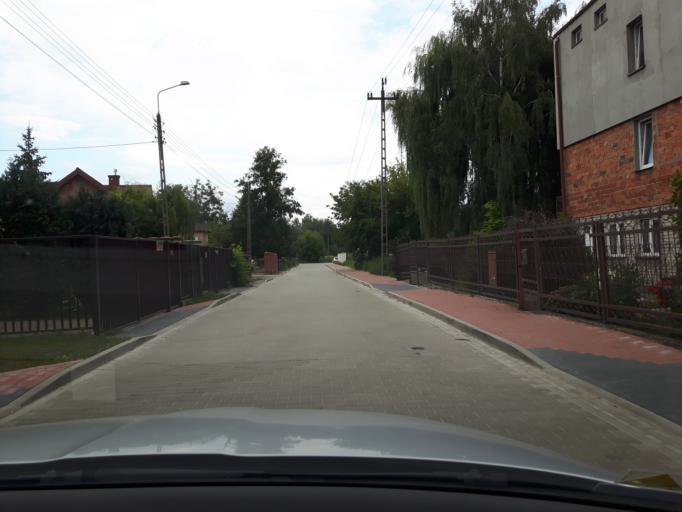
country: PL
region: Masovian Voivodeship
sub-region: Powiat wolominski
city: Zabki
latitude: 52.2888
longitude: 21.1010
